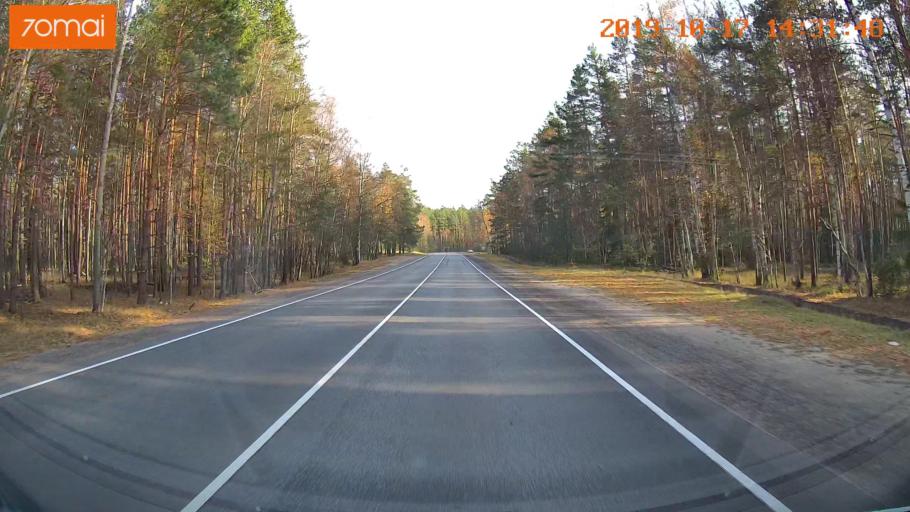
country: RU
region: Rjazan
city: Solotcha
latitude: 54.9333
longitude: 39.9707
